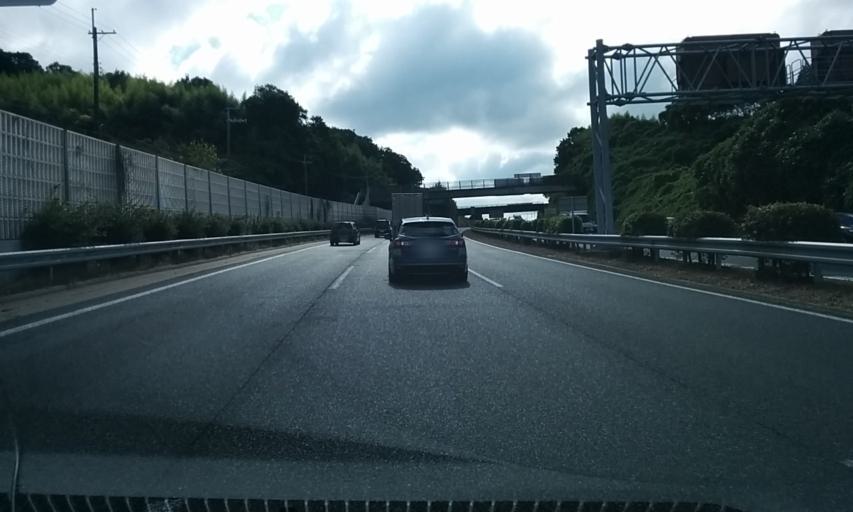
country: JP
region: Hyogo
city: Sandacho
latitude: 34.8908
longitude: 135.1591
